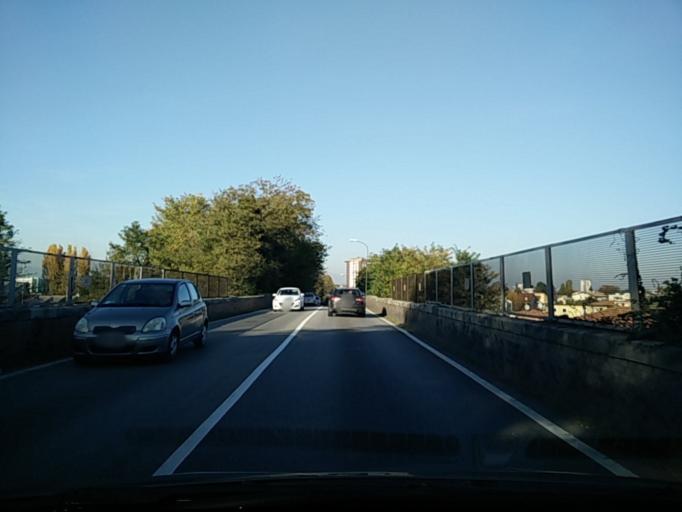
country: IT
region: Veneto
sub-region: Provincia di Treviso
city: Treviso
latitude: 45.6634
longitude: 12.2221
